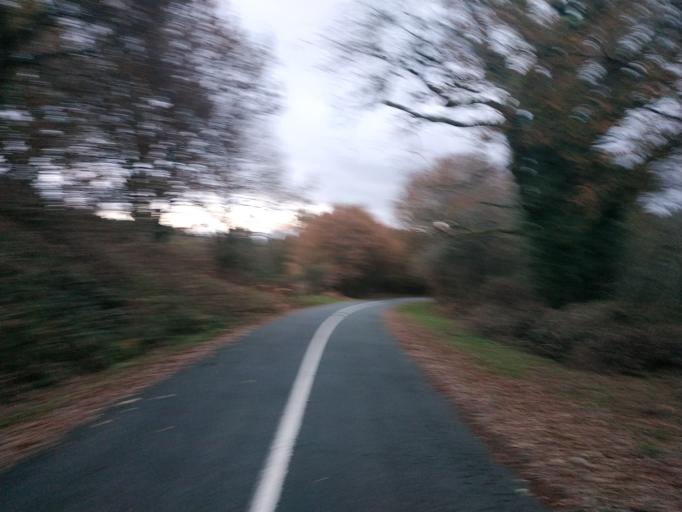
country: ES
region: Galicia
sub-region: Provincia de Pontevedra
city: Silleda
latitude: 42.7764
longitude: -8.1792
